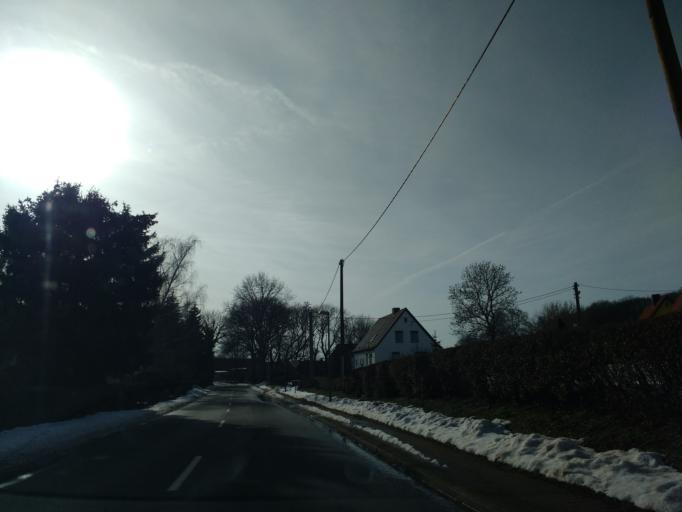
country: DE
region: Saxony-Anhalt
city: Gutenberg
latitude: 51.5495
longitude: 11.9763
